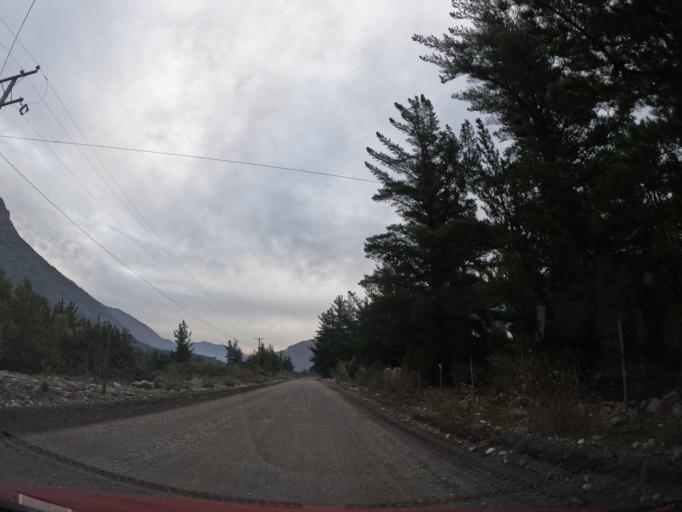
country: CL
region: Maule
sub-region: Provincia de Linares
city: Colbun
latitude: -35.7044
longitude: -71.0878
